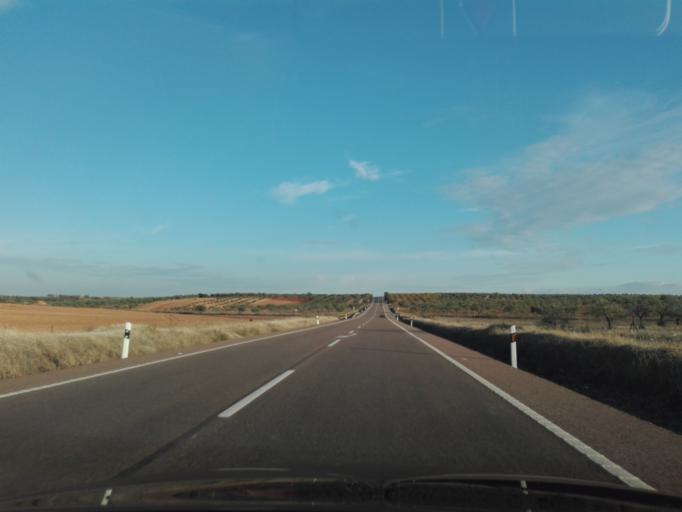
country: ES
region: Extremadura
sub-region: Provincia de Badajoz
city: Usagre
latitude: 38.3487
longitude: -6.1893
